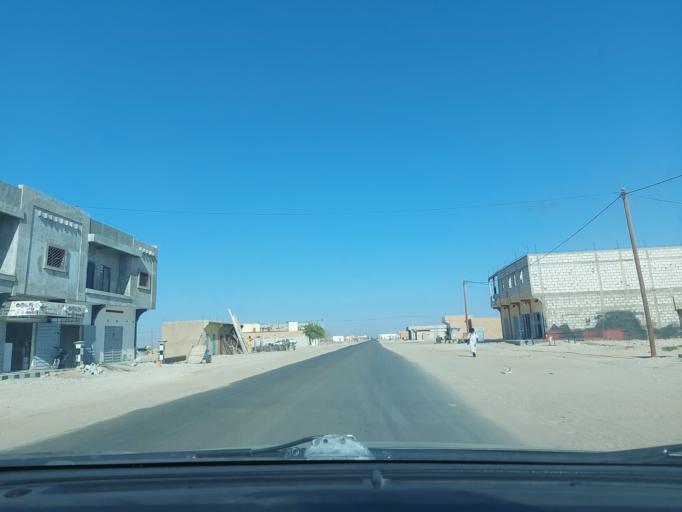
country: MR
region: Nouakchott
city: Nouakchott
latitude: 18.0106
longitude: -15.9797
